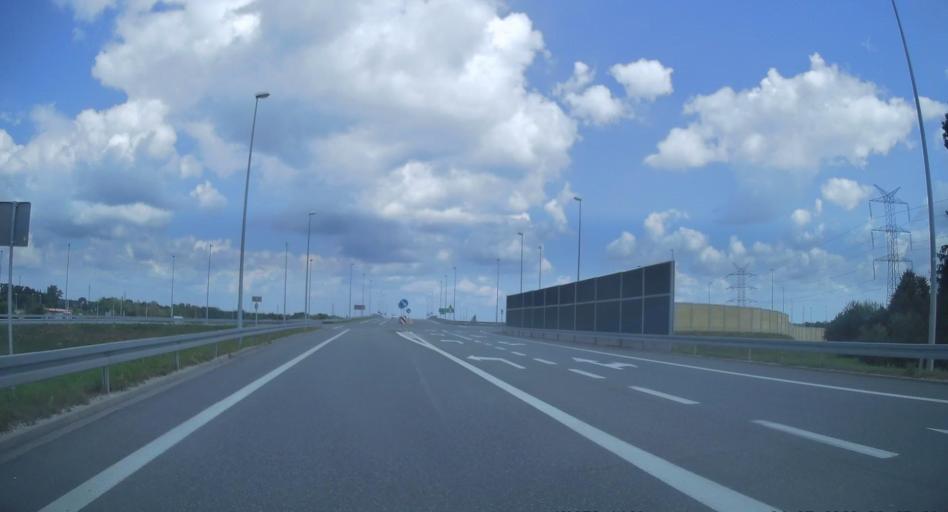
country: PL
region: Lesser Poland Voivodeship
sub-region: Powiat tarnowski
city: Wojnicz
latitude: 49.9613
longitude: 20.8505
